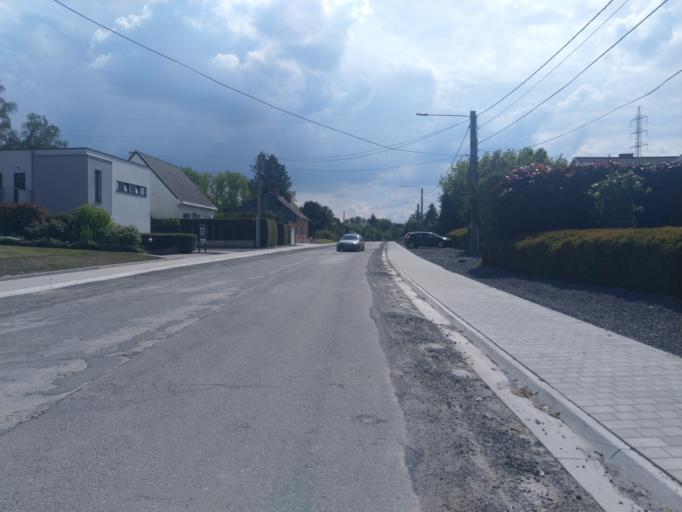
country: BE
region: Wallonia
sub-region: Province du Hainaut
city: Chasse Royale
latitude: 50.4089
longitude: 3.9659
